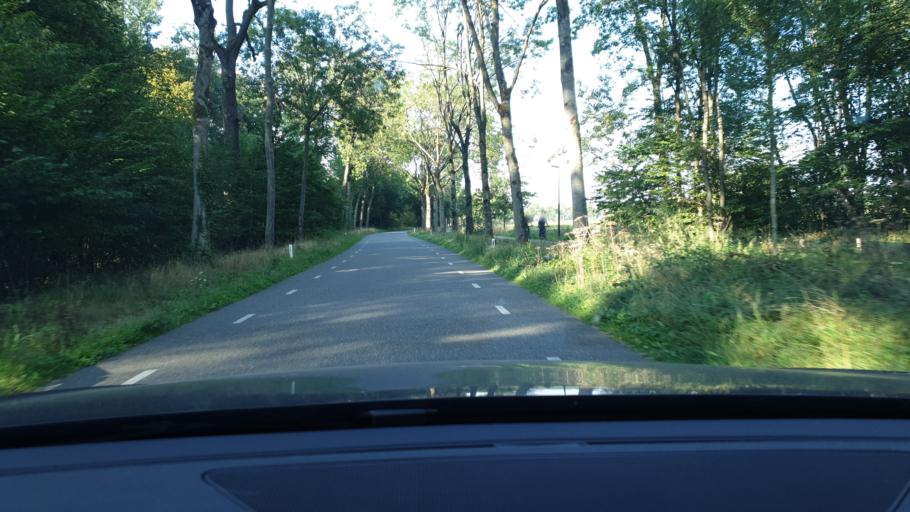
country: NL
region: Limburg
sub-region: Gemeente Maasgouw
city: Maasbracht
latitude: 51.0890
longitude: 5.8591
